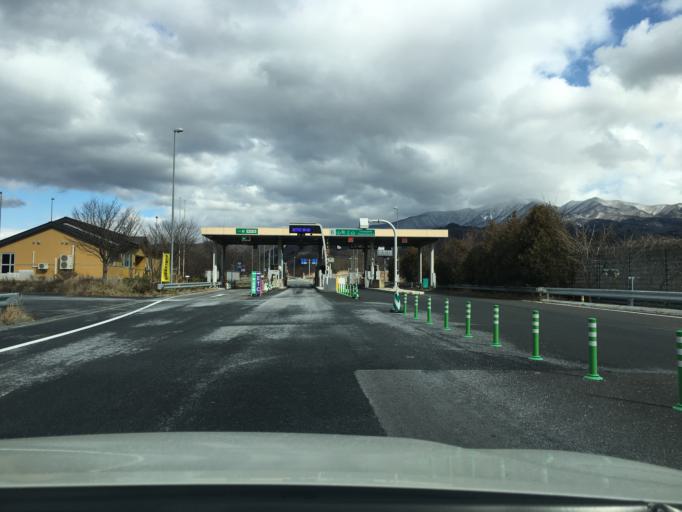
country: JP
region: Yamagata
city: Kaminoyama
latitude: 38.1872
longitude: 140.3061
